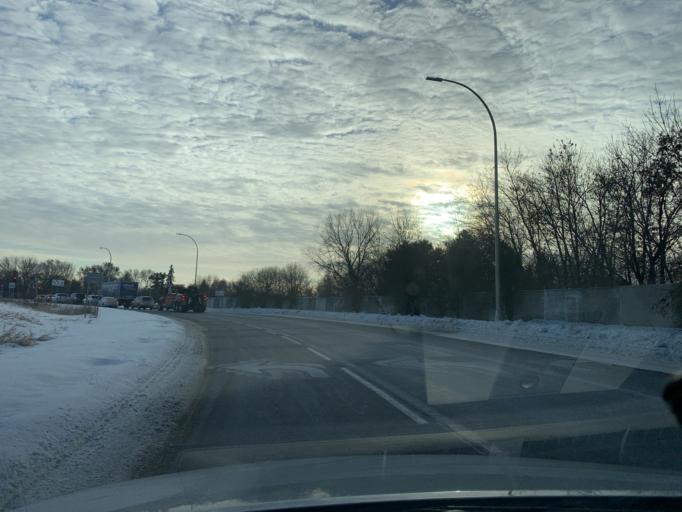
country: US
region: Minnesota
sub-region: Hennepin County
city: Minnetonka Mills
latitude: 44.9357
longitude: -93.3987
